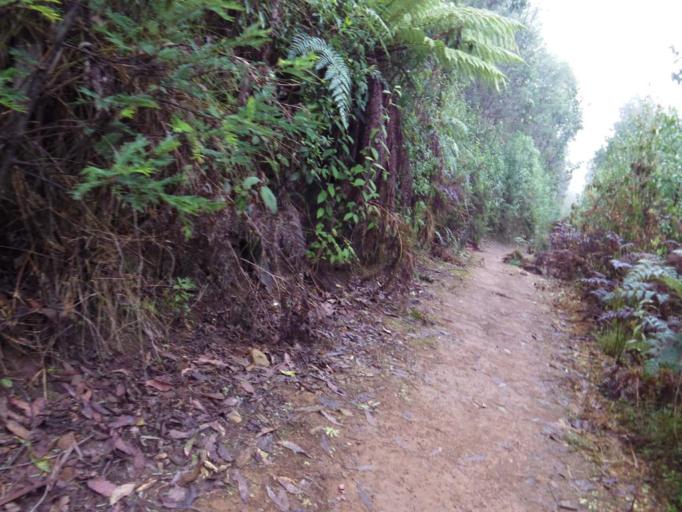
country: AU
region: Victoria
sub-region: Yarra Ranges
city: Millgrove
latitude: -37.5375
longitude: 145.7614
